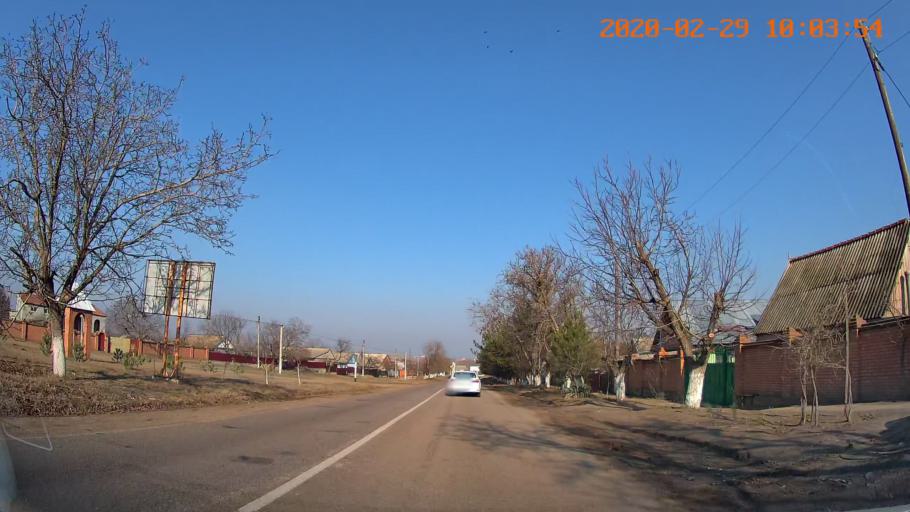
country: MD
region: Causeni
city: Chitcani
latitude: 46.7939
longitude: 29.6784
